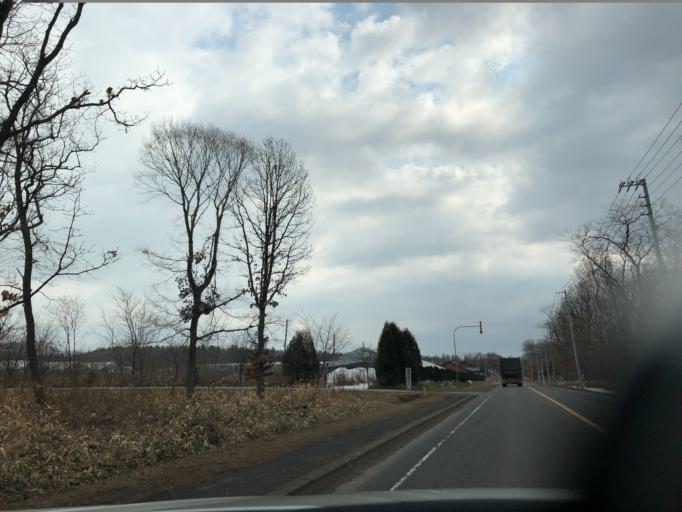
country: JP
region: Hokkaido
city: Chitose
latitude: 42.7609
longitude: 141.7801
